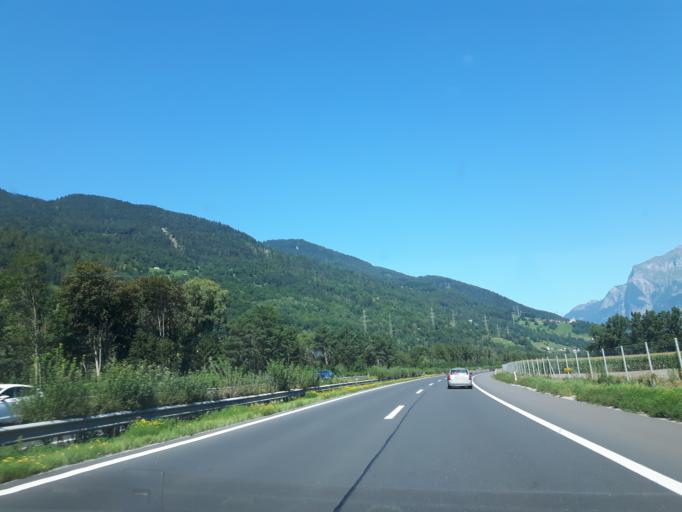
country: CH
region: Grisons
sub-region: Landquart District
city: Zizers
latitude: 46.9423
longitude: 9.5467
